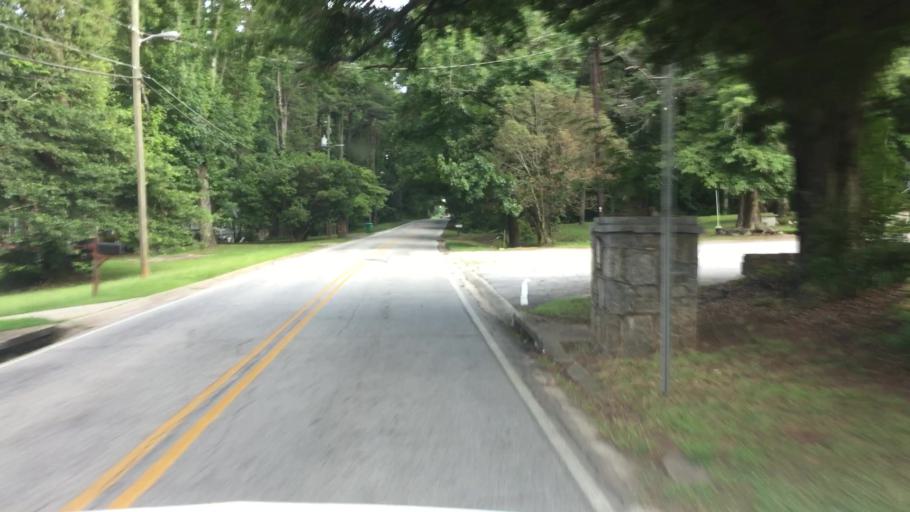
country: US
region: Georgia
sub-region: DeKalb County
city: Lithonia
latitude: 33.7067
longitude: -84.1092
